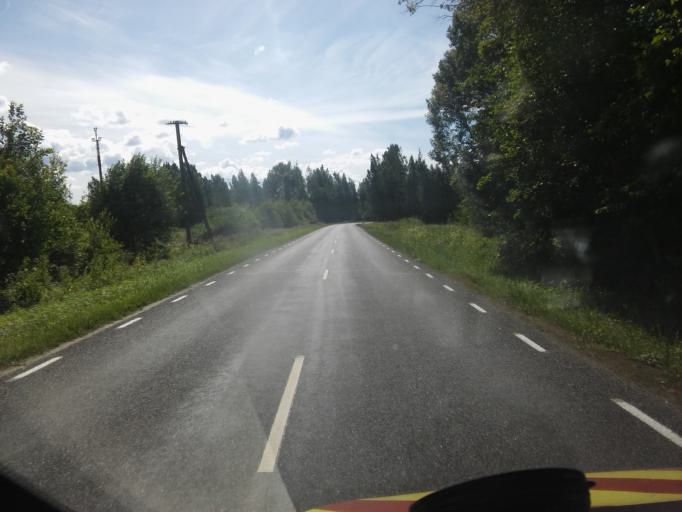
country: EE
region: Paernumaa
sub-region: Paikuse vald
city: Paikuse
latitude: 58.3131
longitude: 24.6872
